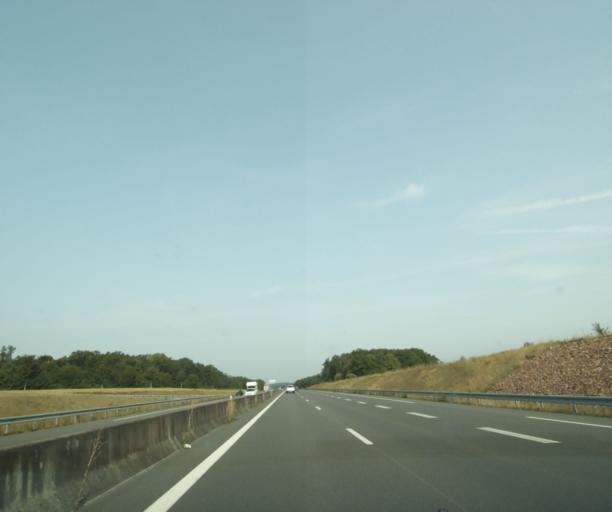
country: FR
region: Pays de la Loire
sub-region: Departement de la Sarthe
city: Champfleur
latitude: 48.3140
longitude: 0.1368
